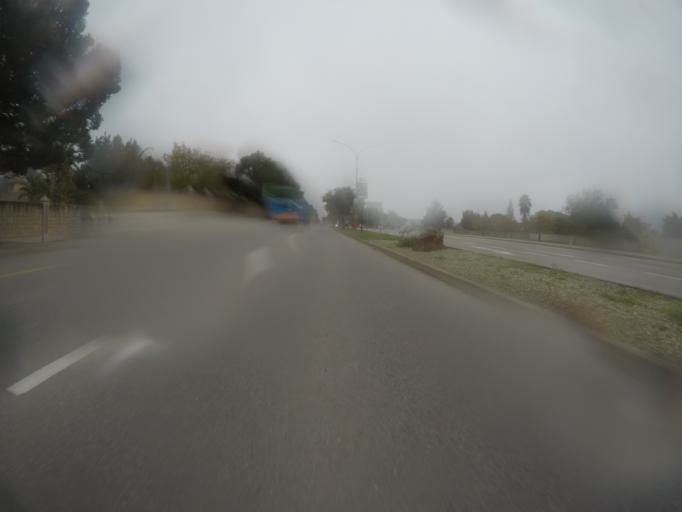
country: ZA
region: Western Cape
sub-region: Eden District Municipality
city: George
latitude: -33.9776
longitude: 22.4420
